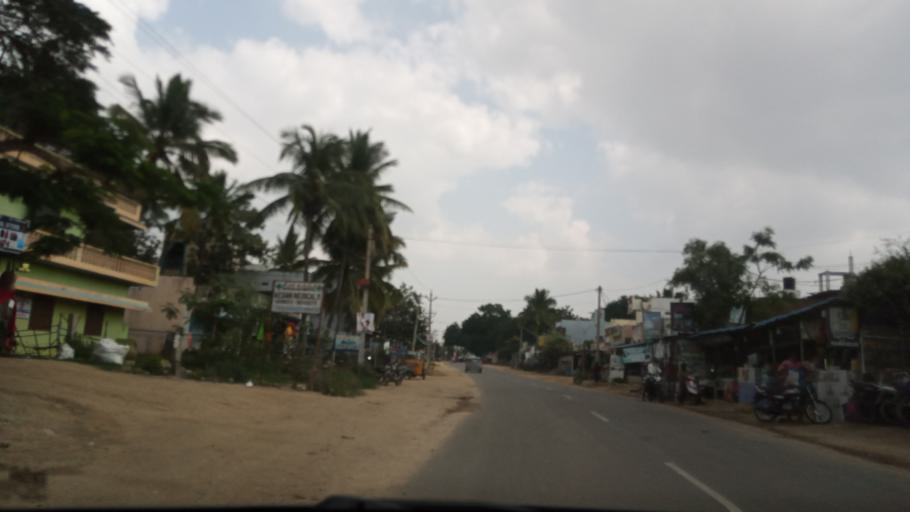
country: IN
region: Andhra Pradesh
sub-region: Chittoor
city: Madanapalle
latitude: 13.6438
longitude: 78.5668
